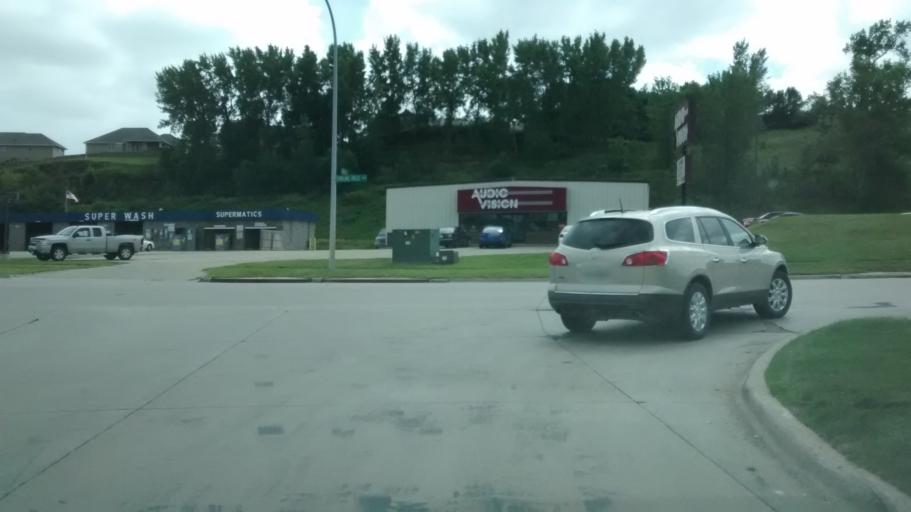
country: US
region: Iowa
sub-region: Woodbury County
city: Sergeant Bluff
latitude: 42.4382
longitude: -96.3501
